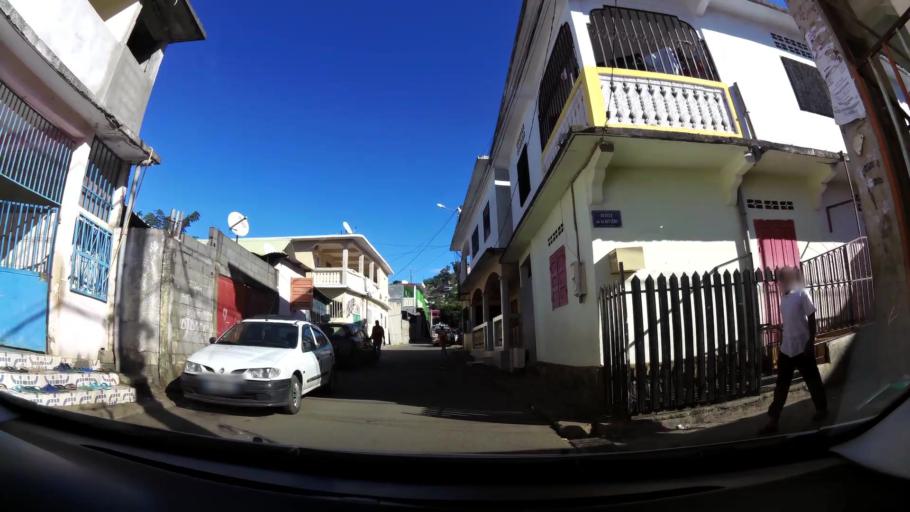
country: YT
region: Mamoudzou
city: Mamoudzou
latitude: -12.7720
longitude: 45.2202
